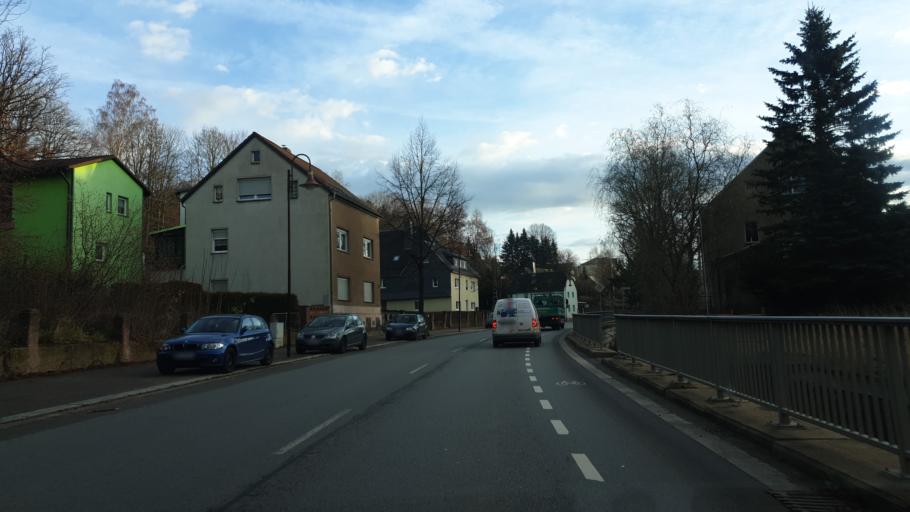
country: DE
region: Saxony
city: Oberlungwitz
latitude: 50.7842
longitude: 12.7133
